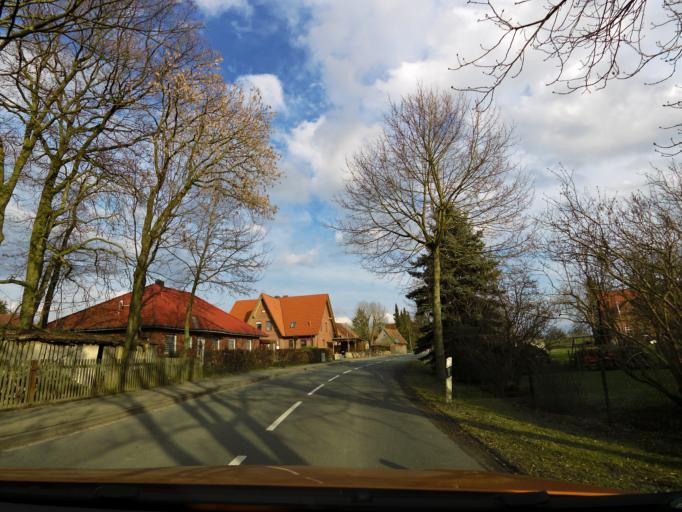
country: DE
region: Lower Saxony
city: Gilten
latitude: 52.7040
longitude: 9.5681
